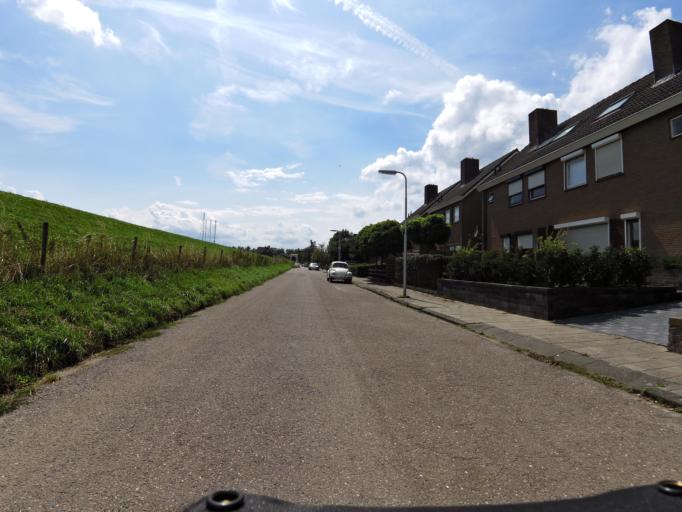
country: NL
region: South Holland
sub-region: Gemeente Strijen
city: Strijen
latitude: 51.7159
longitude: 4.5883
